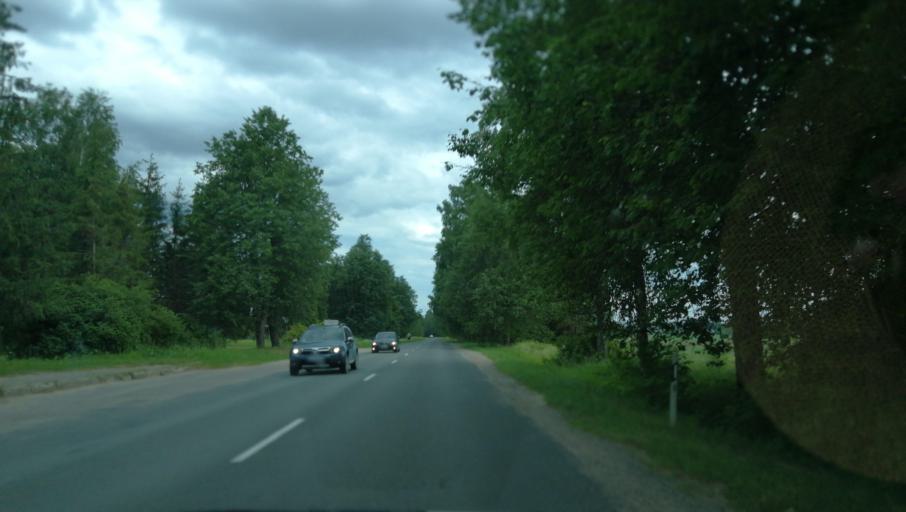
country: LV
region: Rujienas
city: Rujiena
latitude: 57.8786
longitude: 25.3591
